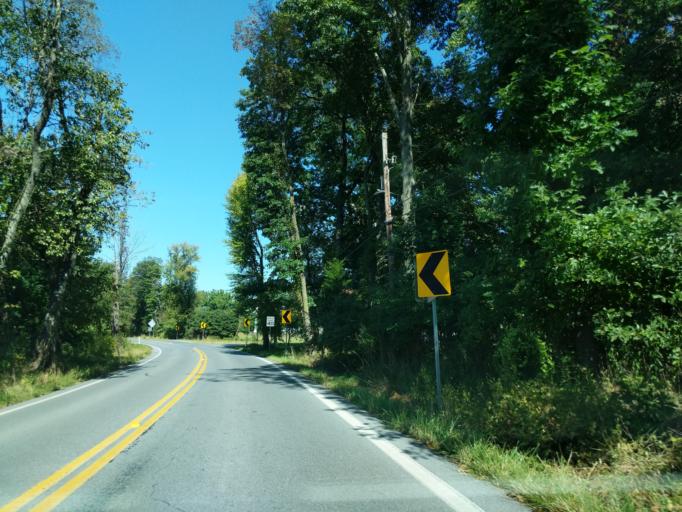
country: US
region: Pennsylvania
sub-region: Montgomery County
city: East Greenville
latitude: 40.4446
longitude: -75.4881
